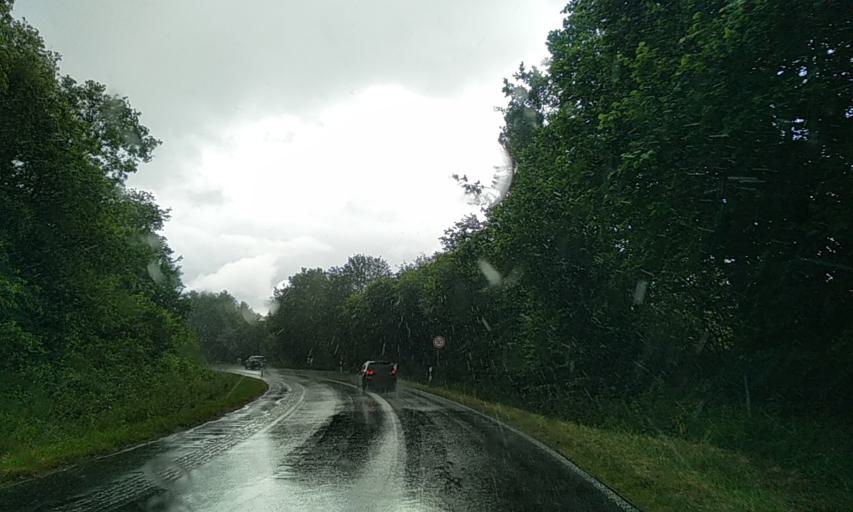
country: DE
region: Schleswig-Holstein
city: Lurschau
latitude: 54.5477
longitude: 9.4908
